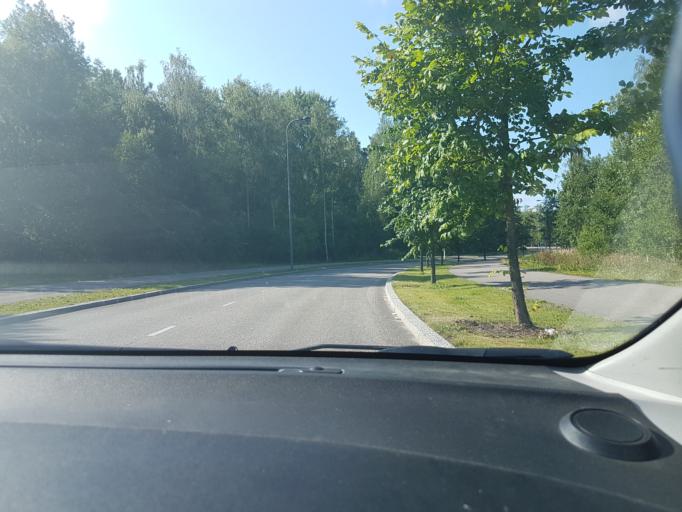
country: FI
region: Uusimaa
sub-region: Helsinki
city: Vantaa
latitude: 60.3323
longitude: 25.0277
